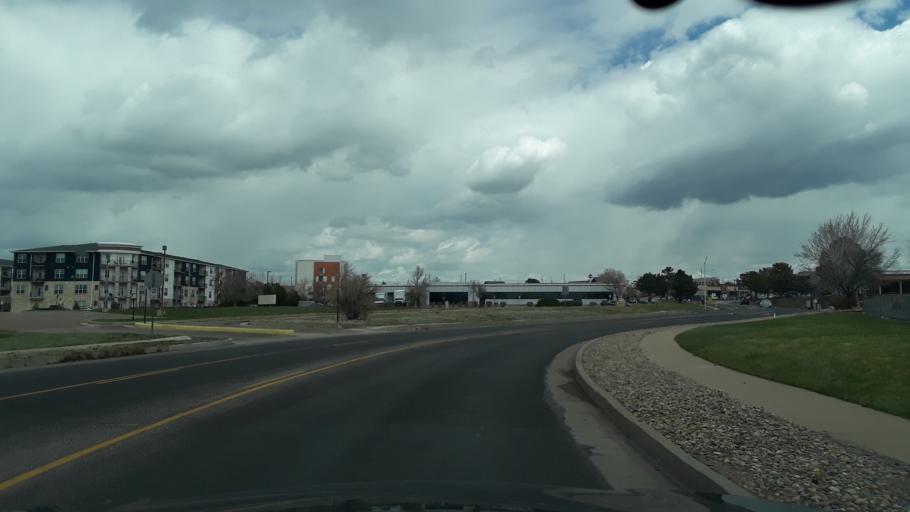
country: US
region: Colorado
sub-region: El Paso County
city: Air Force Academy
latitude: 38.9443
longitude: -104.8042
